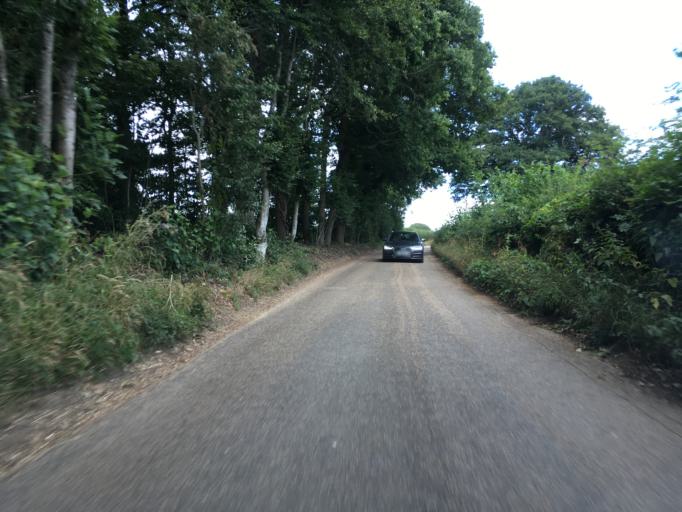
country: GB
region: England
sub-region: Kent
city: Cranbrook
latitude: 51.1129
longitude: 0.5732
